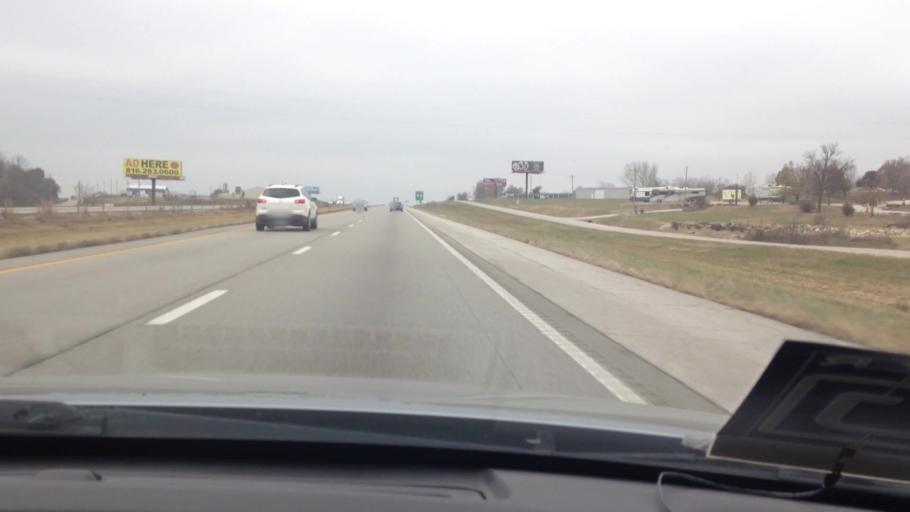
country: US
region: Missouri
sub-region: Cass County
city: Peculiar
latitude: 38.7044
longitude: -94.4373
